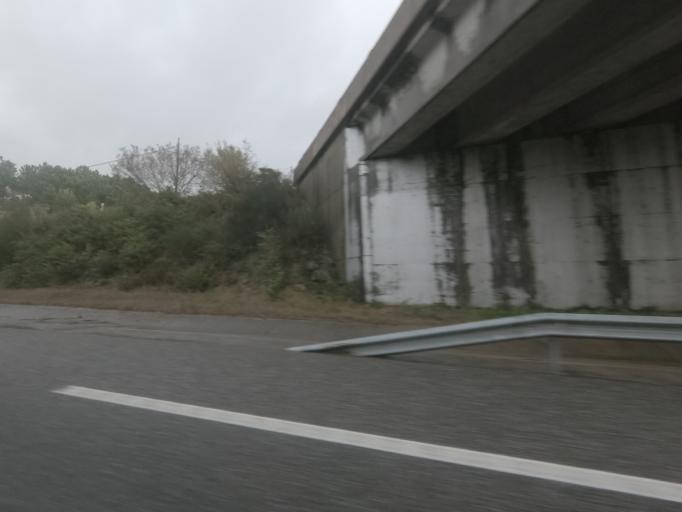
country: ES
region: Galicia
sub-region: Provincia de Pontevedra
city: Porrino
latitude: 42.1976
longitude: -8.6652
